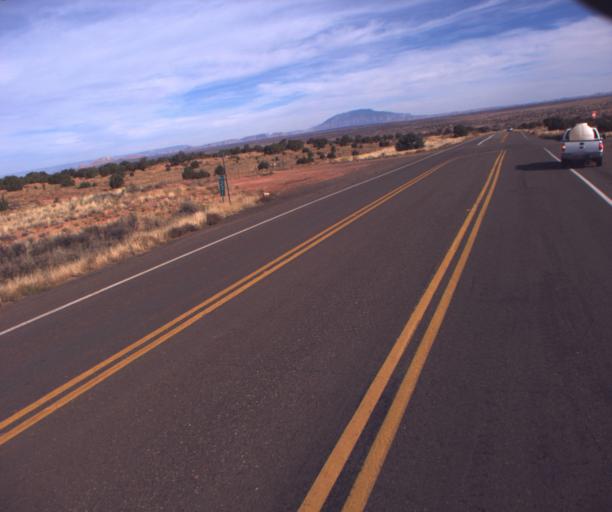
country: US
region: Arizona
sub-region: Coconino County
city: Kaibito
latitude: 36.5947
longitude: -111.0962
